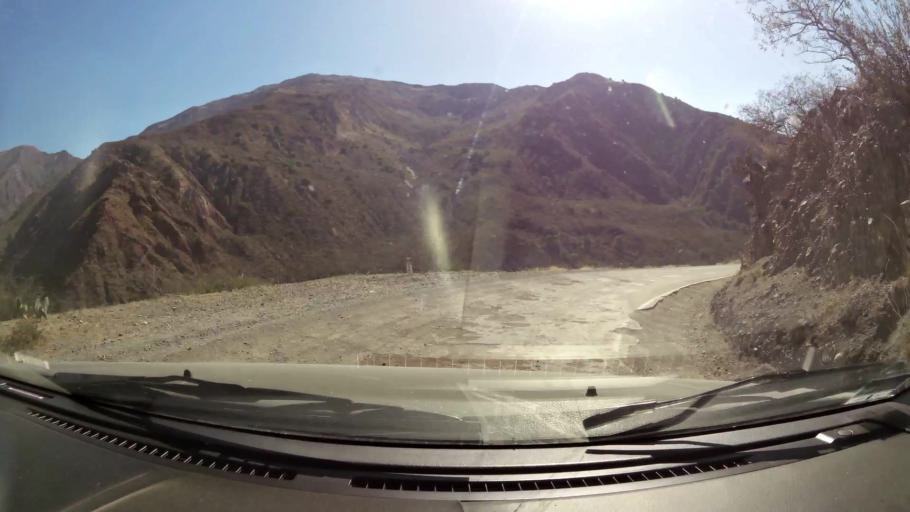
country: PE
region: Huancavelica
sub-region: Provincia de Acobamba
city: Pomacocha
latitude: -12.7876
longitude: -74.4979
